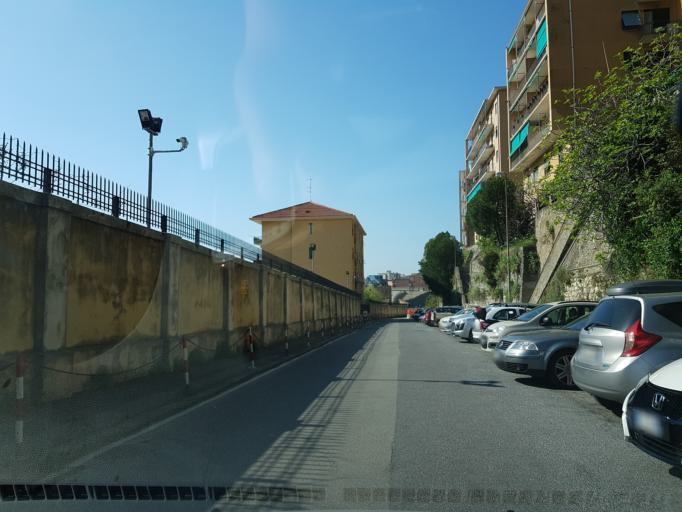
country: IT
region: Liguria
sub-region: Provincia di Genova
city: Genoa
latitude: 44.3985
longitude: 8.9850
